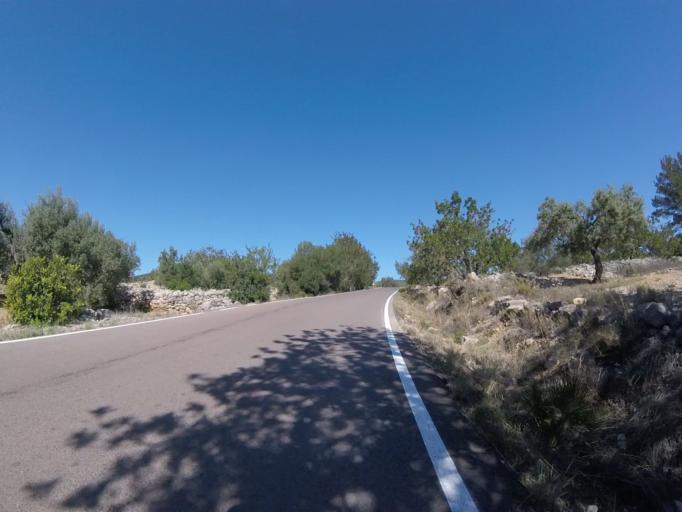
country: ES
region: Valencia
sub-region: Provincia de Castello
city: Santa Magdalena de Pulpis
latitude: 40.3740
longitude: 0.2721
